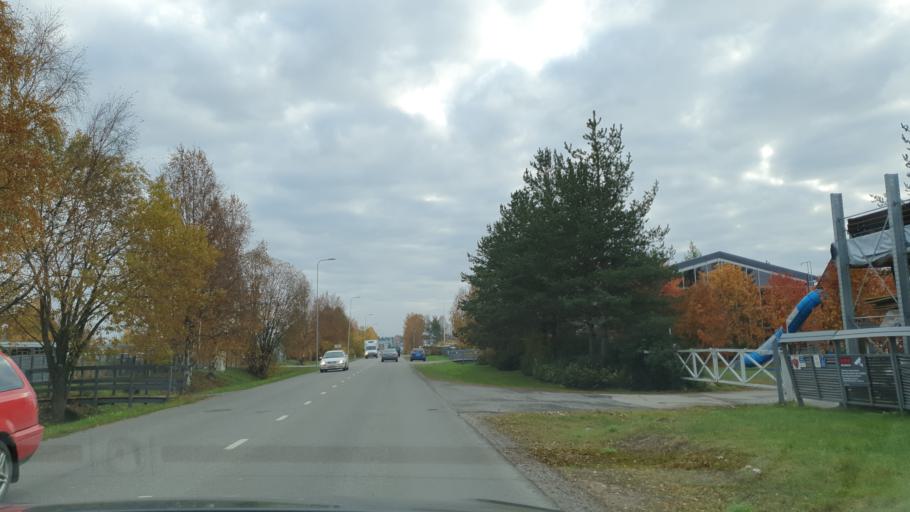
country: FI
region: Lapland
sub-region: Rovaniemi
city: Rovaniemi
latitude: 66.4946
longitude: 25.6728
